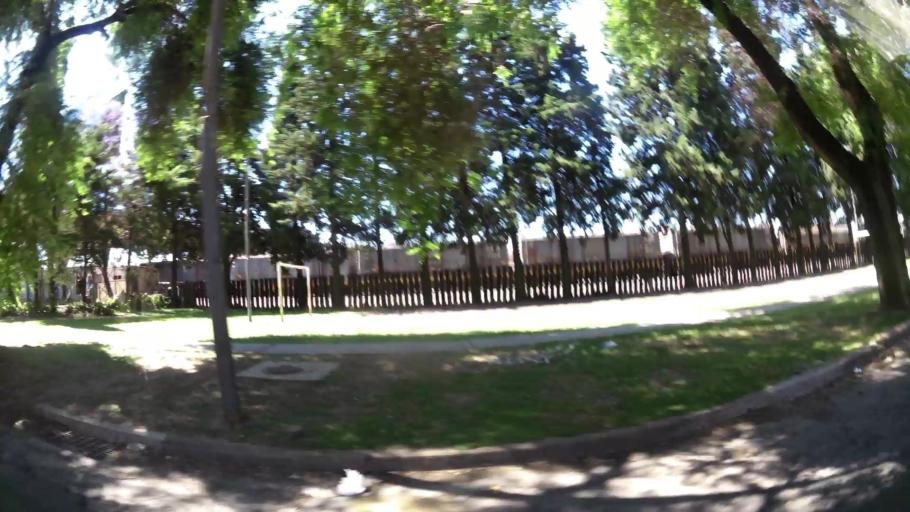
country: AR
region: Santa Fe
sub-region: Departamento de Rosario
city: Rosario
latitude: -32.9335
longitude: -60.6772
